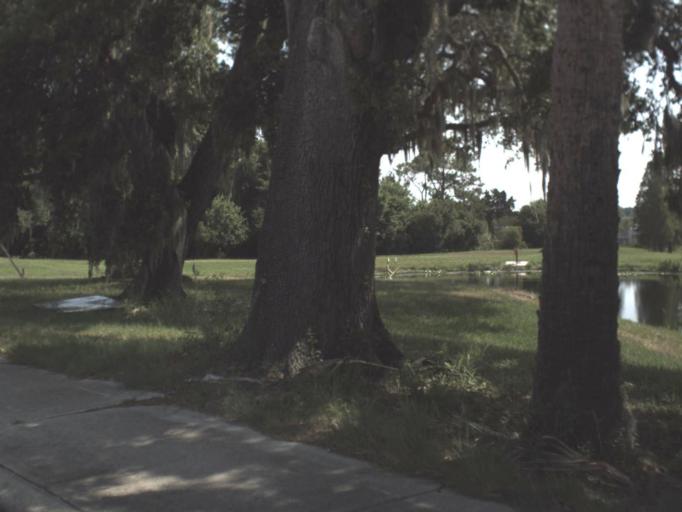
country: US
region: Florida
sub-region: Pinellas County
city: Seminole
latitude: 27.8528
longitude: -82.7870
